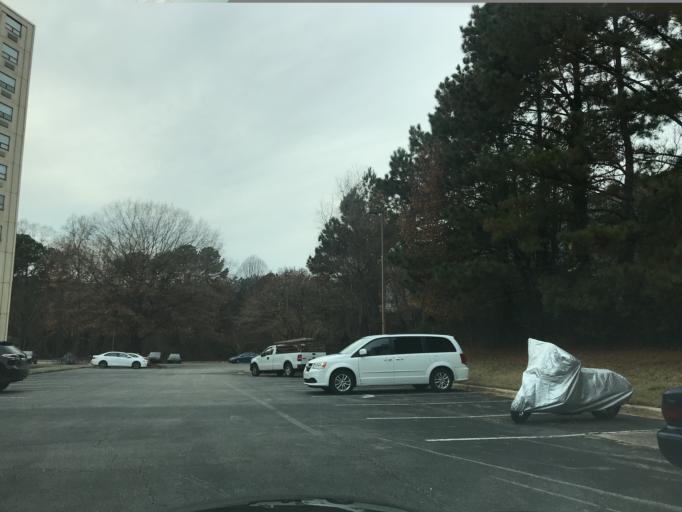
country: US
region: North Carolina
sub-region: Wake County
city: West Raleigh
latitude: 35.7880
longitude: -78.7000
